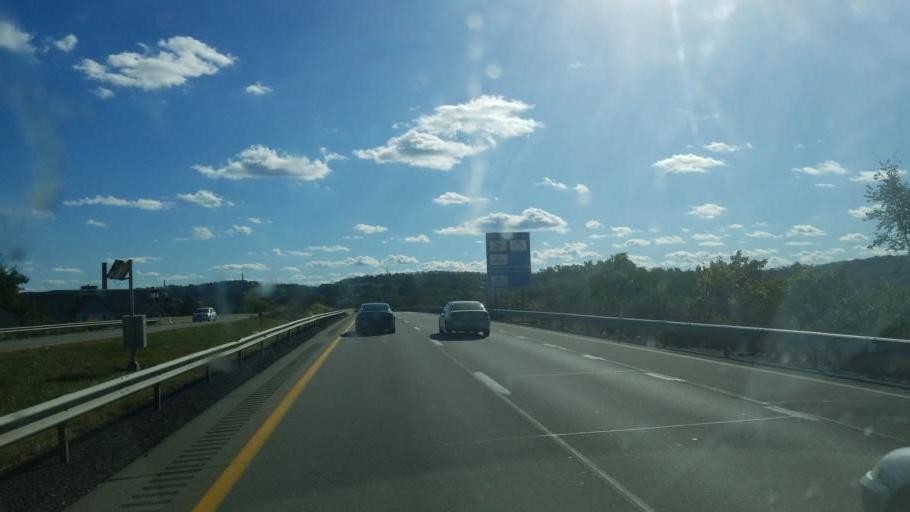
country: US
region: Pennsylvania
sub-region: Washington County
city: Wolfdale
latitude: 40.1718
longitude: -80.2724
